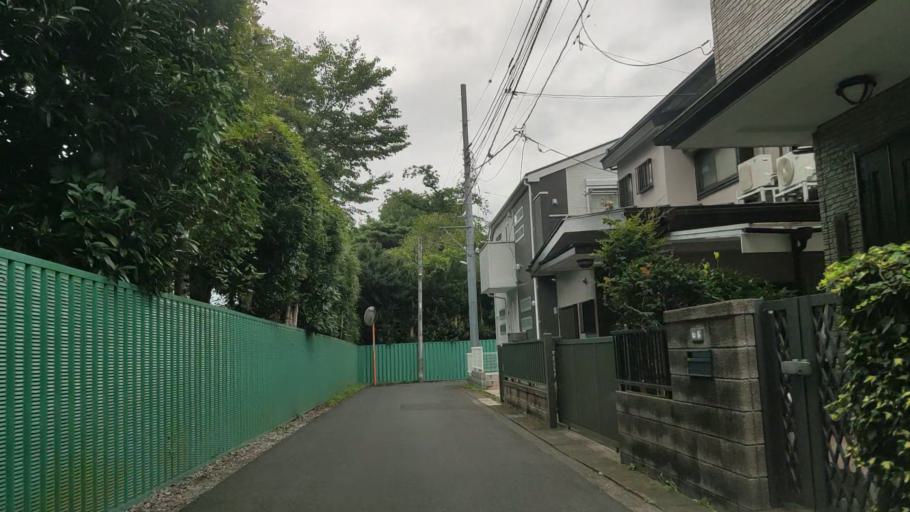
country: JP
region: Kanagawa
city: Minami-rinkan
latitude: 35.5112
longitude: 139.4393
